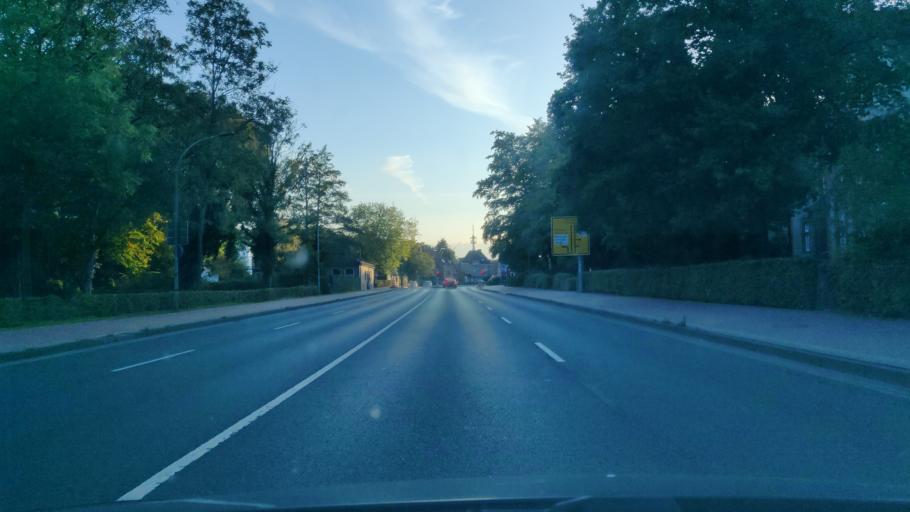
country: DE
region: Lower Saxony
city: Aurich
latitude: 53.4709
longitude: 7.4784
